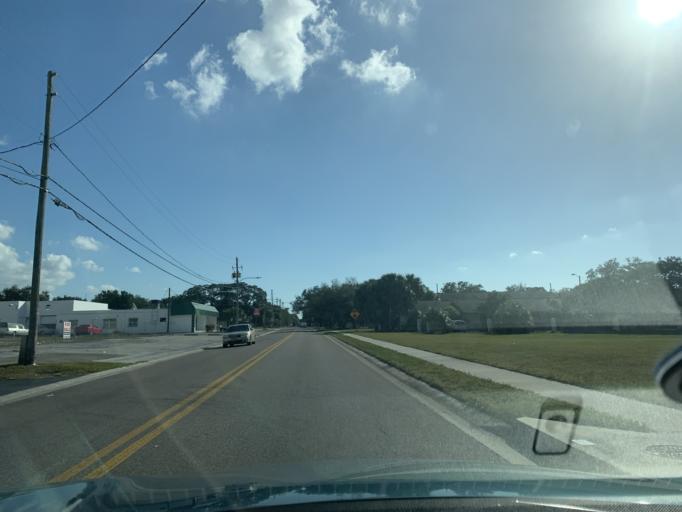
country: US
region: Florida
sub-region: Pinellas County
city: Belleair
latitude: 27.9442
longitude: -82.7917
